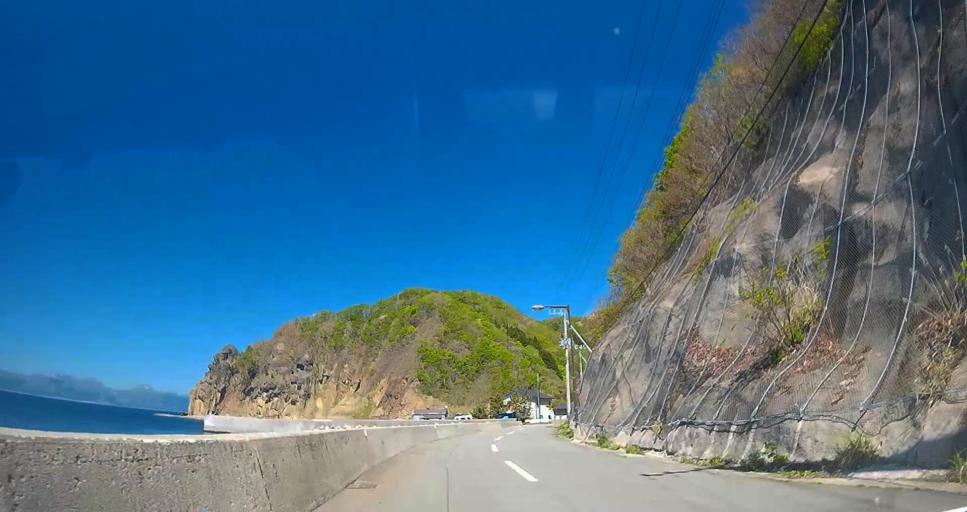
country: JP
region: Aomori
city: Aomori Shi
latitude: 41.1400
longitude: 140.7744
